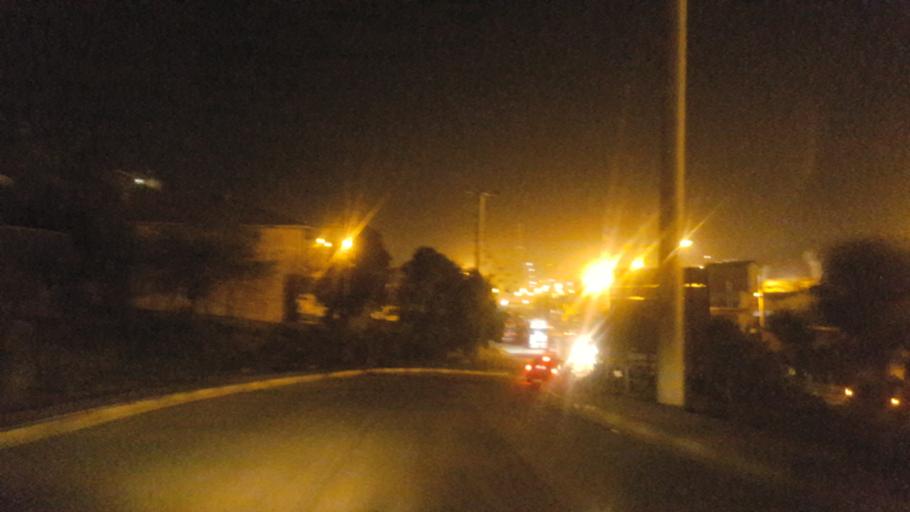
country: TR
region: Kocaeli
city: Tavsancil
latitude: 40.7723
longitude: 29.5243
